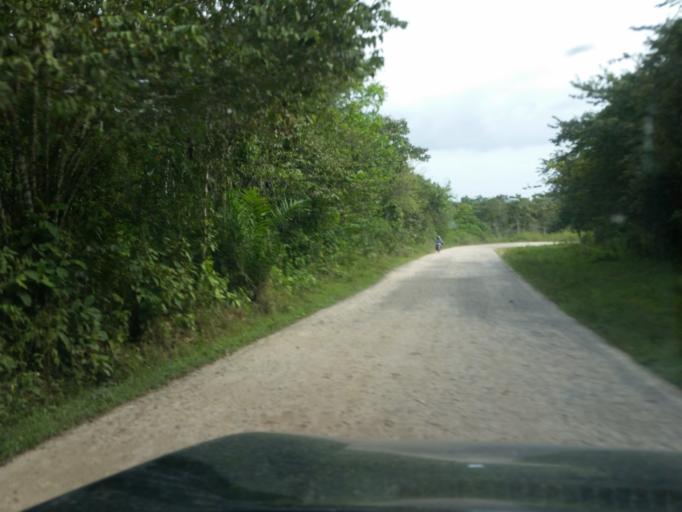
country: CR
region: Alajuela
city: Los Chiles
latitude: 11.1405
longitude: -84.6091
